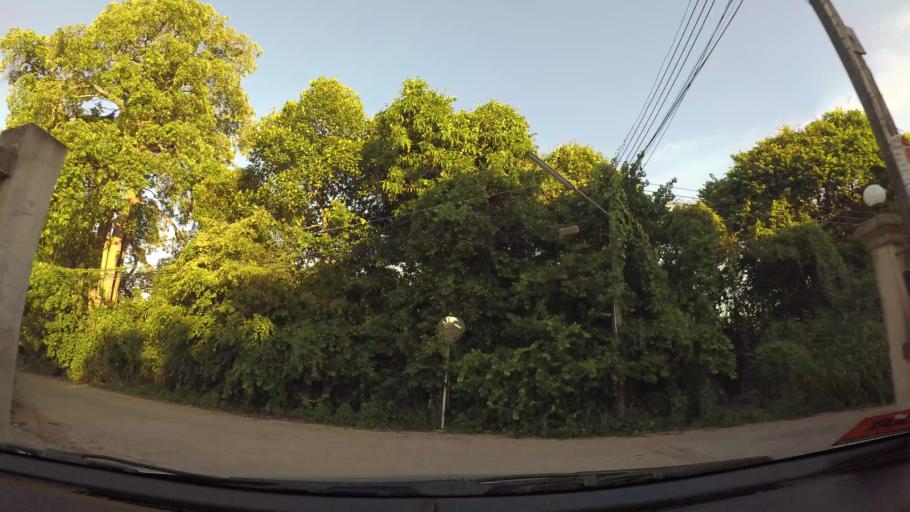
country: TH
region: Chon Buri
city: Si Racha
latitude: 13.1308
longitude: 100.9391
